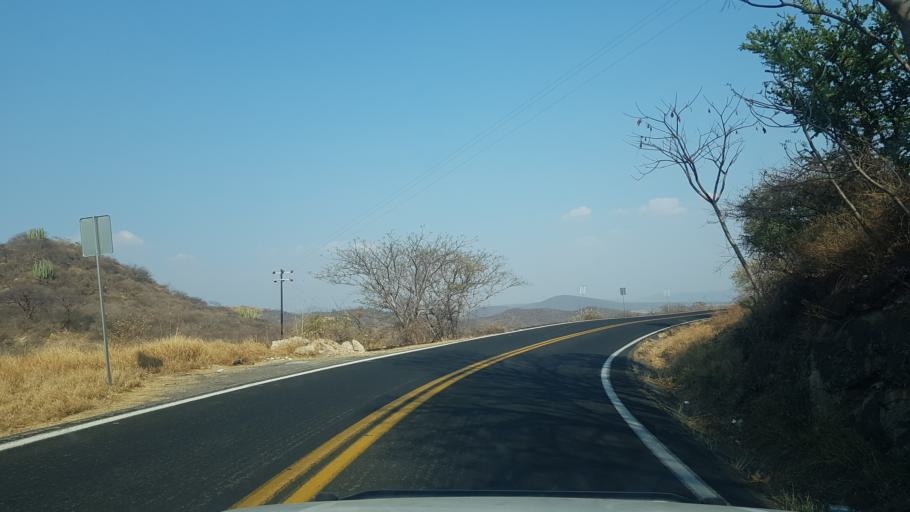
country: MX
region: Puebla
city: Calmeca
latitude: 18.6461
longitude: -98.5994
